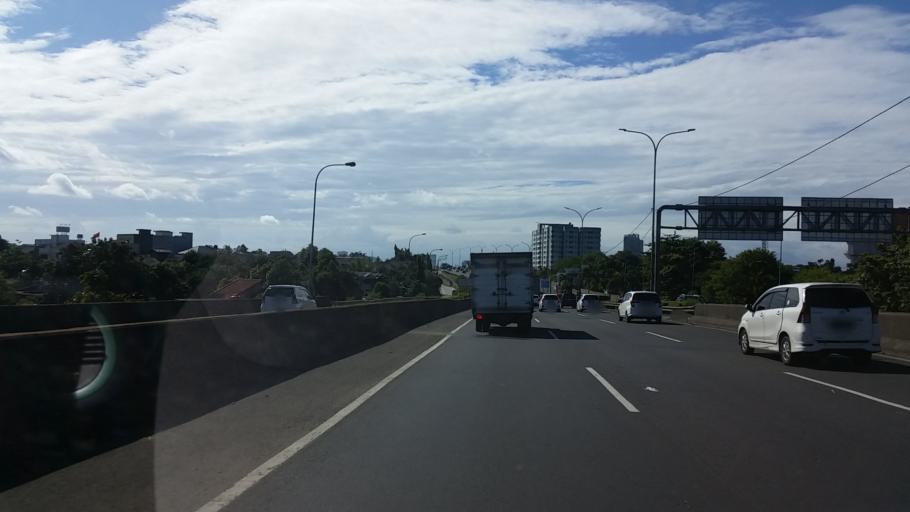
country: ID
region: Banten
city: South Tangerang
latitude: -6.2573
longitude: 106.7654
